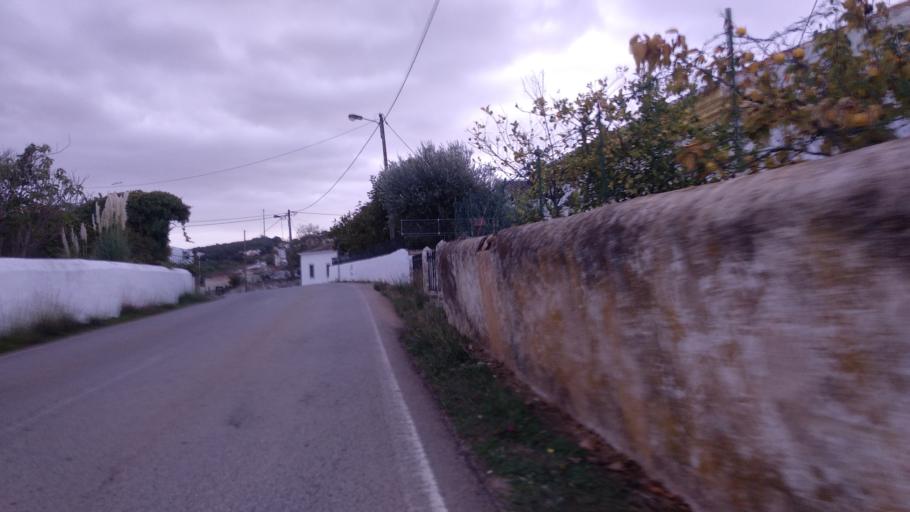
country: PT
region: Faro
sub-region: Sao Bras de Alportel
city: Sao Bras de Alportel
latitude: 37.1707
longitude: -7.9083
